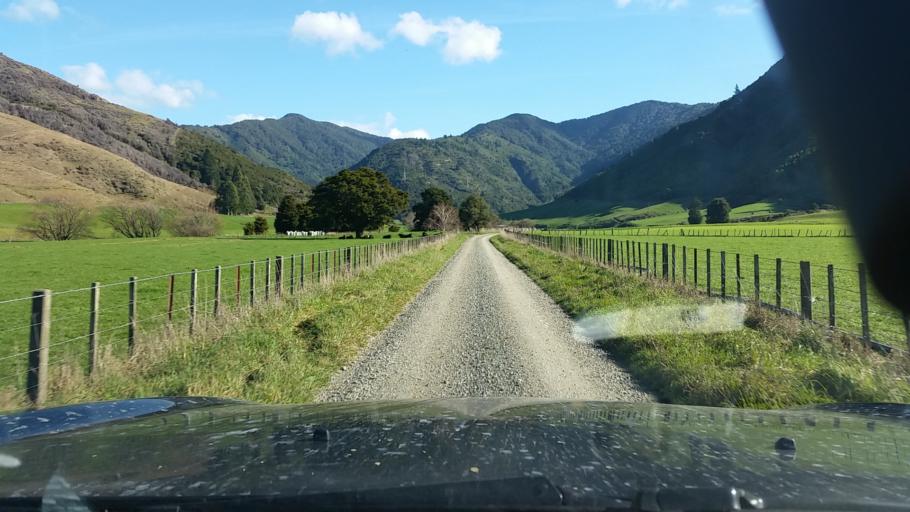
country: NZ
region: Marlborough
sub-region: Marlborough District
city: Picton
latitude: -41.3190
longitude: 173.7590
